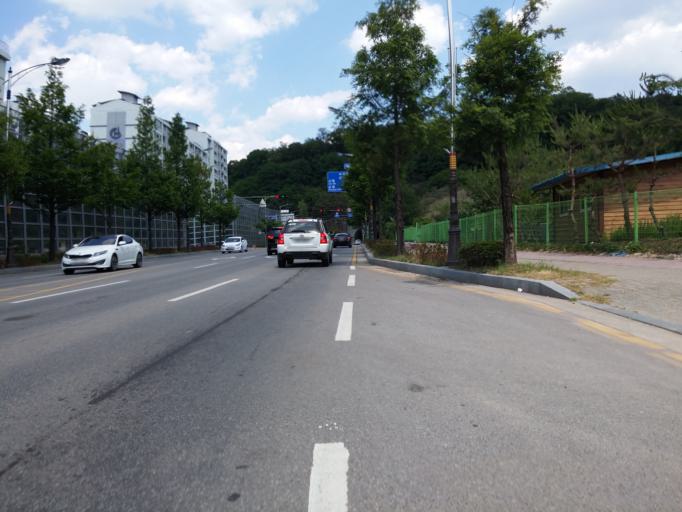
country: KR
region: Chungcheongbuk-do
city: Cheongju-si
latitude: 36.6148
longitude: 127.4579
